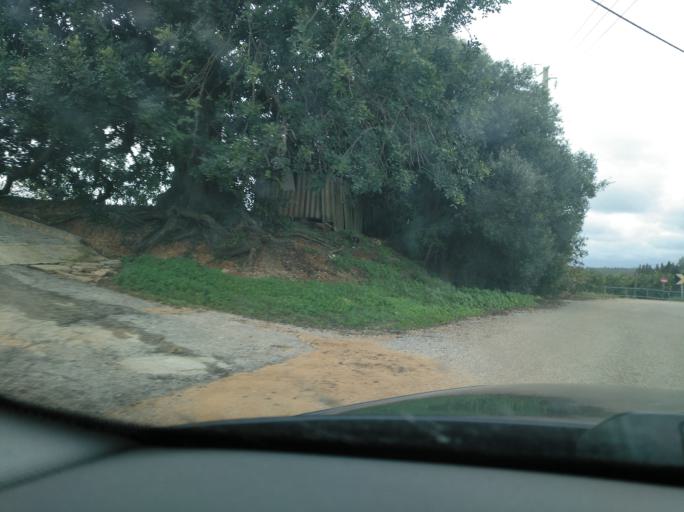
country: PT
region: Faro
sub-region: Vila Real de Santo Antonio
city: Monte Gordo
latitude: 37.1925
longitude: -7.5057
